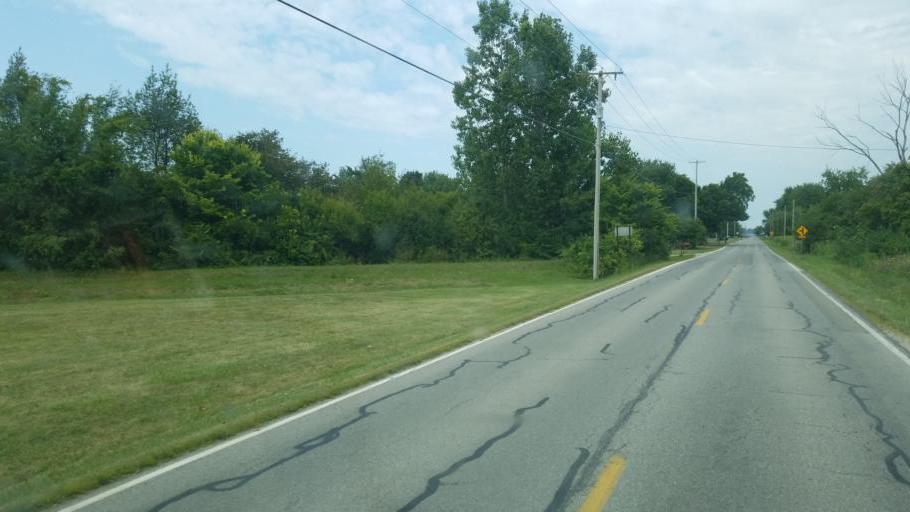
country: US
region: Ohio
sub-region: Marion County
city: Marion
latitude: 40.5682
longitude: -83.1645
